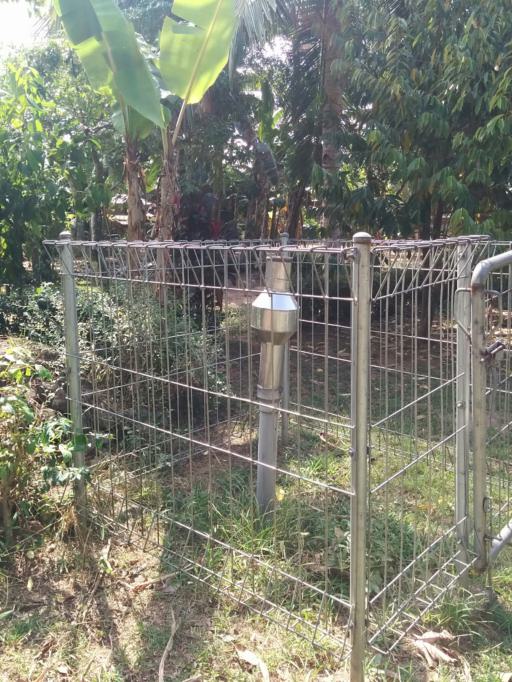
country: ID
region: East Java
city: Sitiarjo
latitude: -8.3788
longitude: 112.6787
